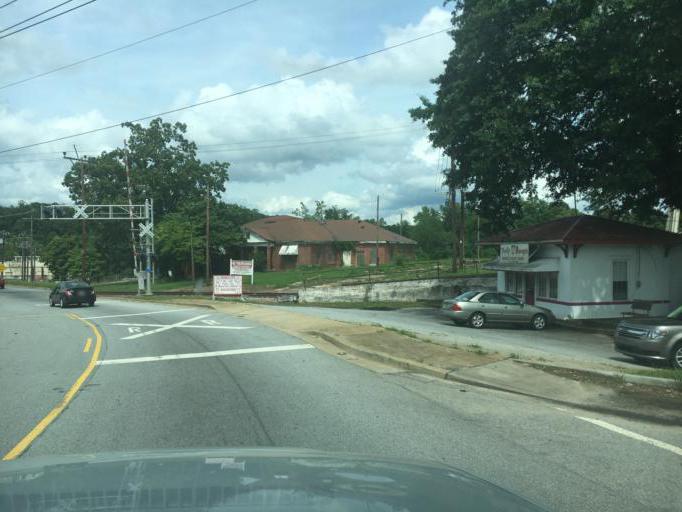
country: US
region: South Carolina
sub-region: Anderson County
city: Williamston
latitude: 34.6418
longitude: -82.4560
